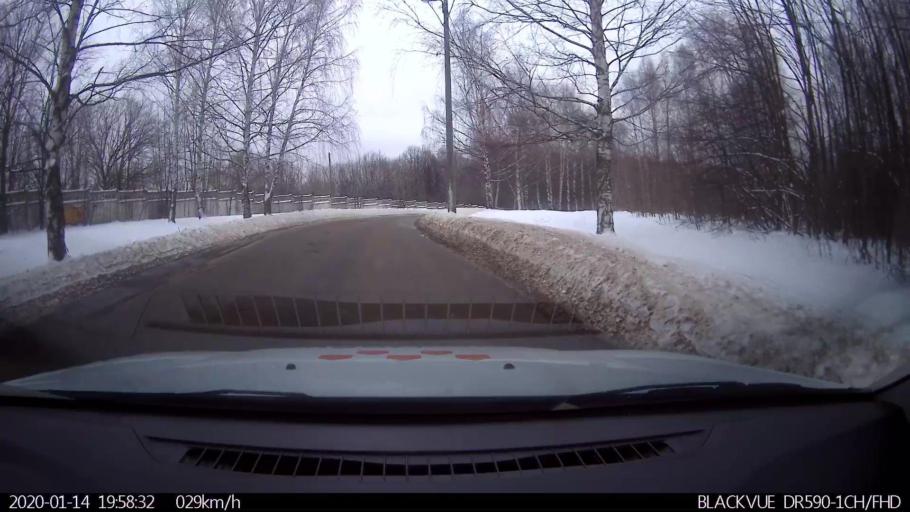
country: RU
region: Nizjnij Novgorod
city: Nizhniy Novgorod
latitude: 56.2377
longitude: 43.9404
